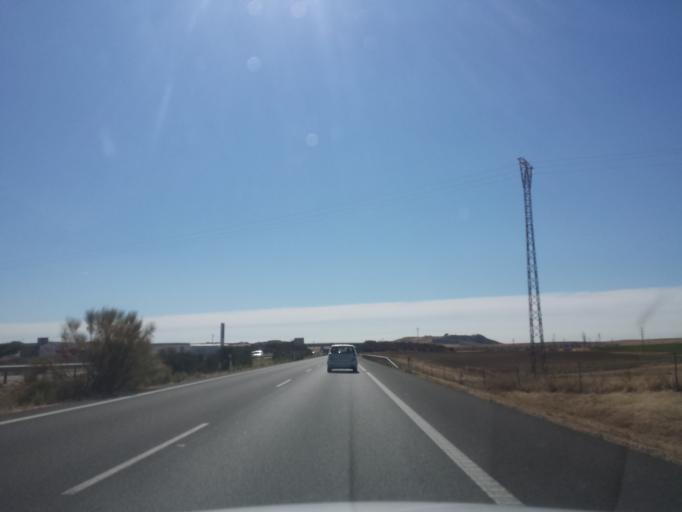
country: ES
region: Castille and Leon
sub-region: Provincia de Valladolid
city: Mota del Marques
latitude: 41.6272
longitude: -5.1775
